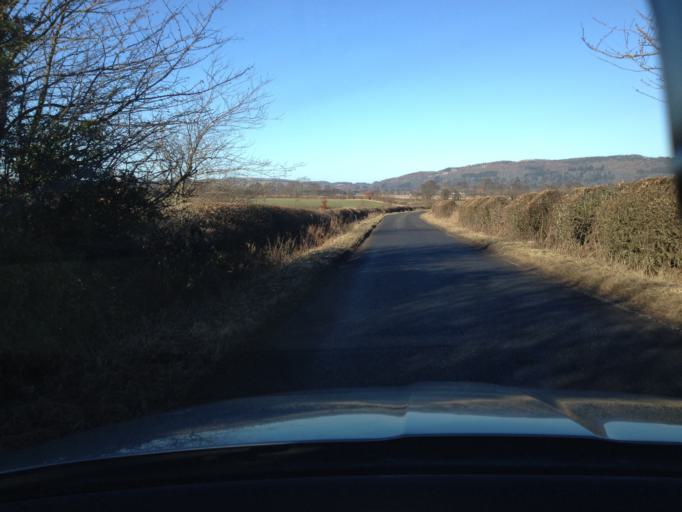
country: GB
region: Scotland
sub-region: Perth and Kinross
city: Bridge of Earn
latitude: 56.3264
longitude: -3.3778
